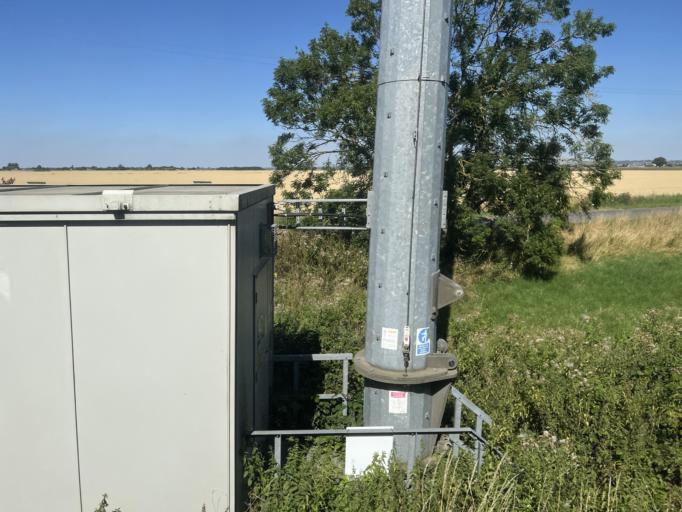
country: GB
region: England
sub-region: Lincolnshire
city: Spilsby
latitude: 53.0835
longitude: 0.0889
